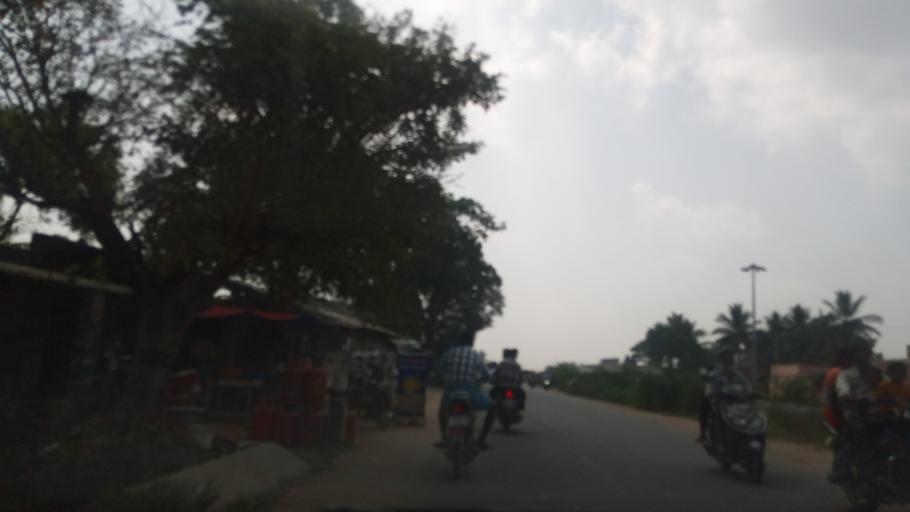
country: IN
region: Tamil Nadu
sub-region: Vellore
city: Arakkonam
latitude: 13.0571
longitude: 79.6741
